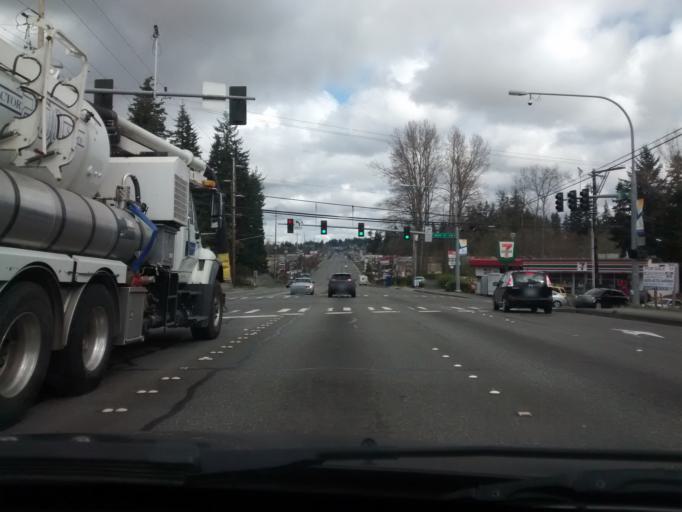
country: US
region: Washington
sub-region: Snohomish County
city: Lynnwood
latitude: 47.8280
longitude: -122.3092
